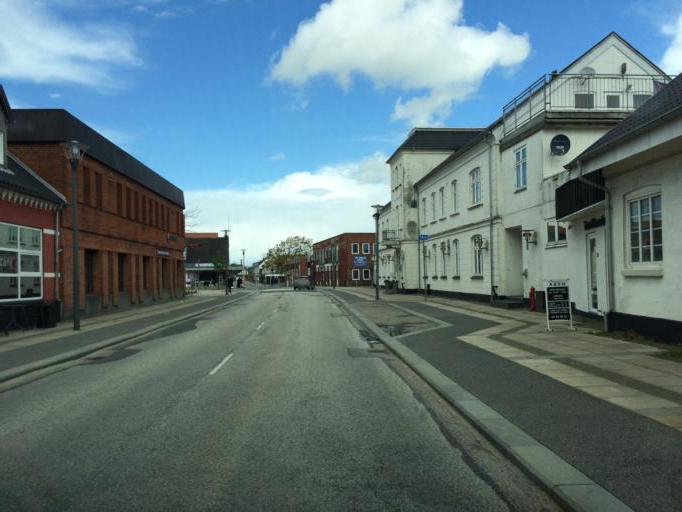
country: DK
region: North Denmark
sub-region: Vesthimmerland Kommune
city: Farso
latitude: 56.7710
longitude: 9.3404
